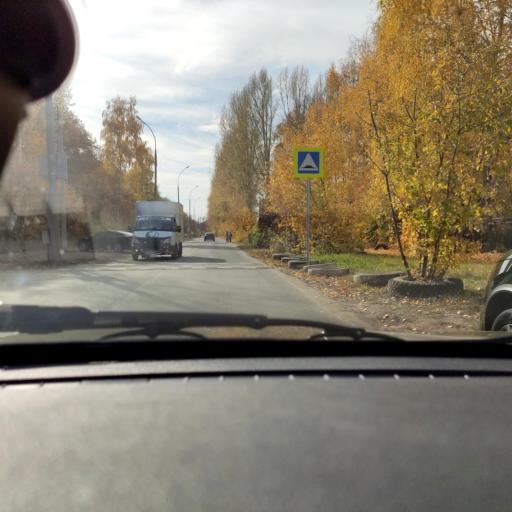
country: RU
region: Samara
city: Tol'yatti
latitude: 53.5053
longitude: 49.3053
